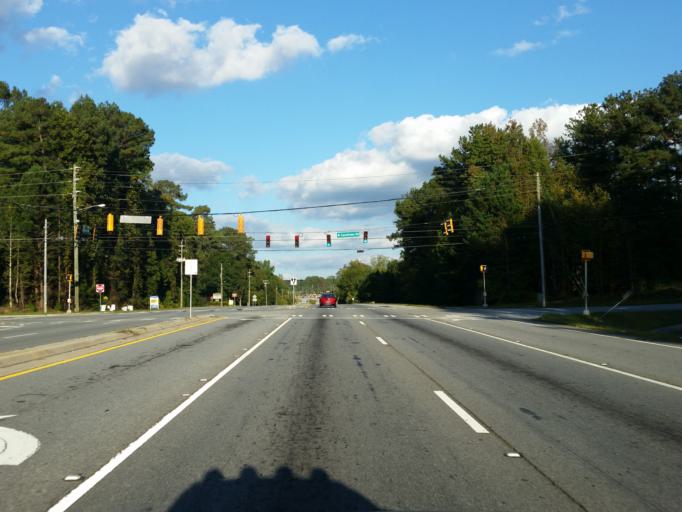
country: US
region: Georgia
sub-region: Cobb County
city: Powder Springs
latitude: 33.8985
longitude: -84.6352
